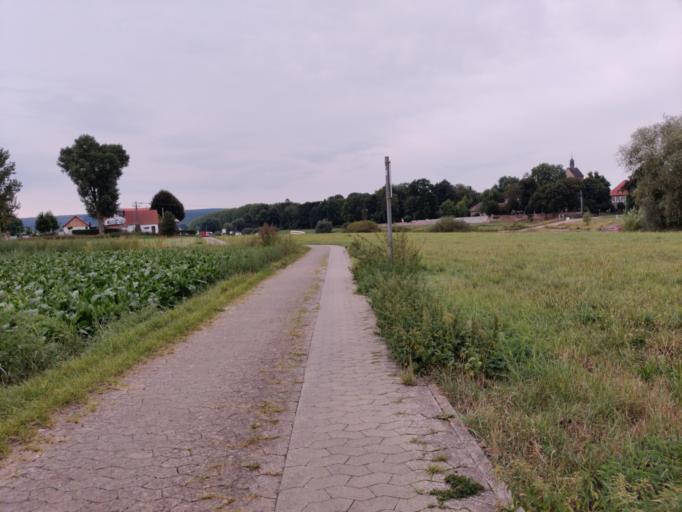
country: DE
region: Lower Saxony
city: Hehlen
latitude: 52.0209
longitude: 9.4259
